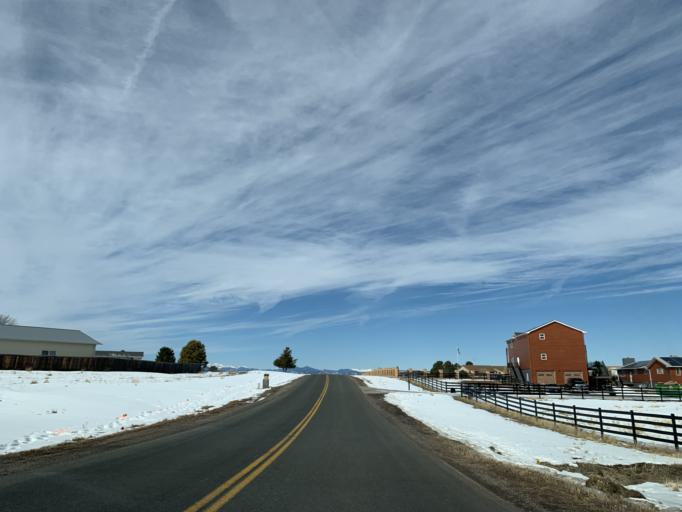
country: US
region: Colorado
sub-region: Douglas County
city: Carriage Club
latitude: 39.5182
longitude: -104.9092
